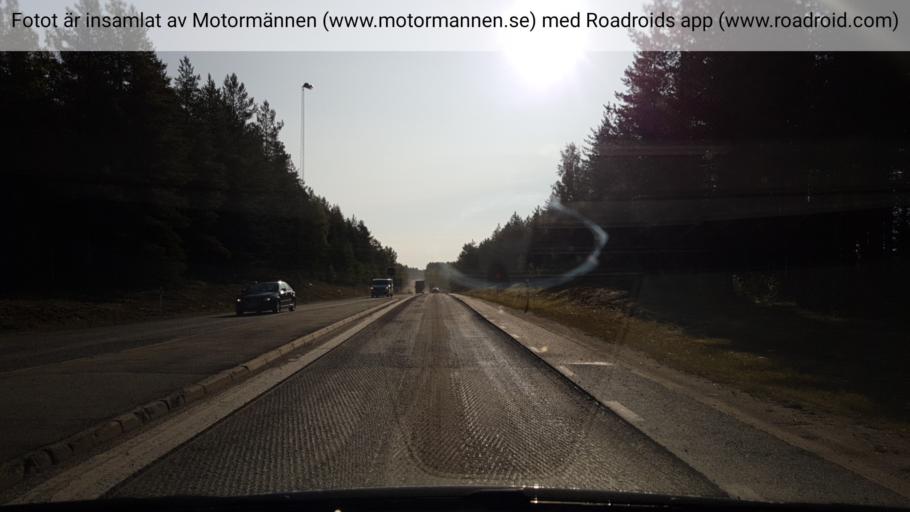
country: SE
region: Vaesterbotten
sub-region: Umea Kommun
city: Roback
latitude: 63.8450
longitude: 20.1621
